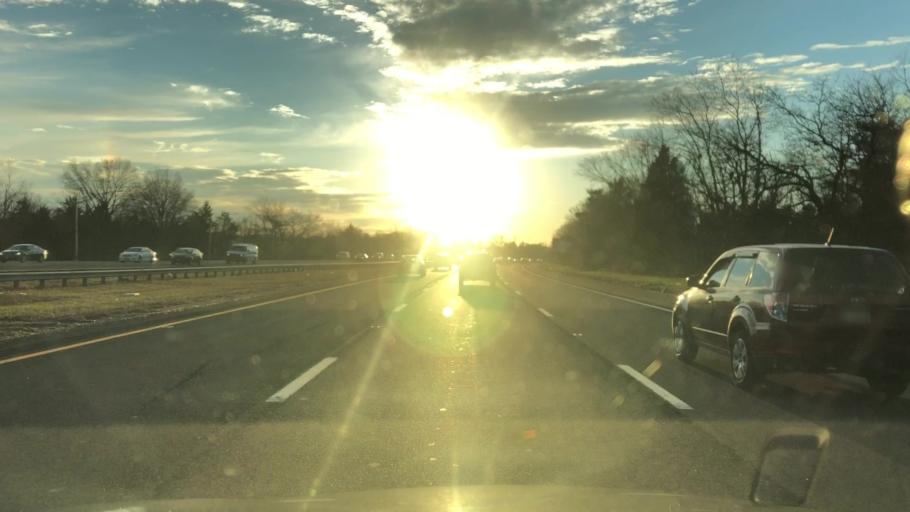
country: US
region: New Jersey
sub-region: Middlesex County
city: Society Hill
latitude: 40.5563
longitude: -74.4386
